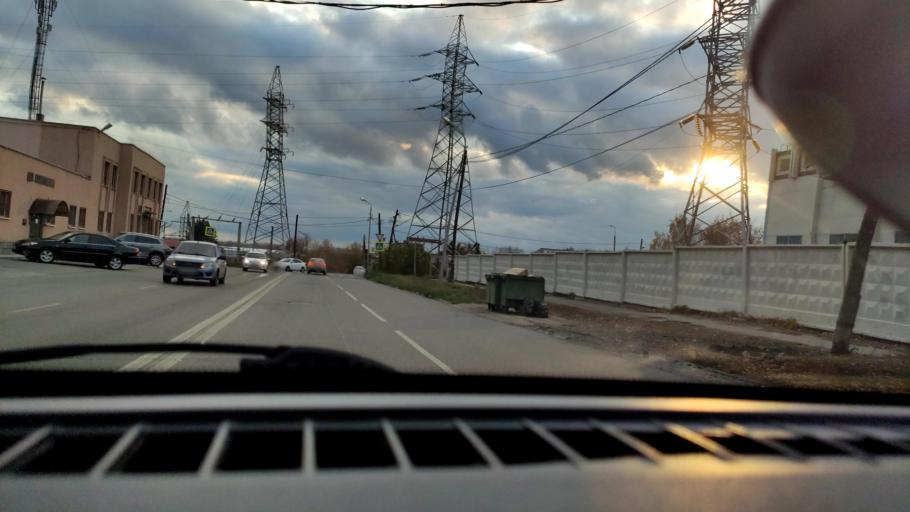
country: RU
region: Samara
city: Samara
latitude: 53.1820
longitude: 50.1055
